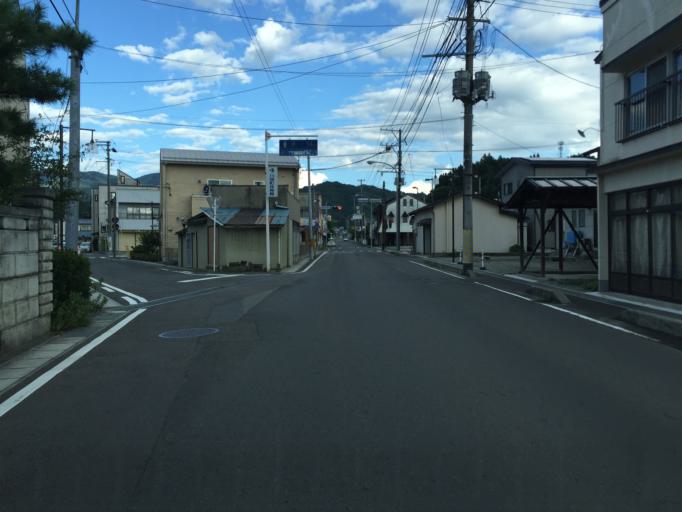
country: JP
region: Fukushima
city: Fukushima-shi
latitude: 37.6655
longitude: 140.5951
